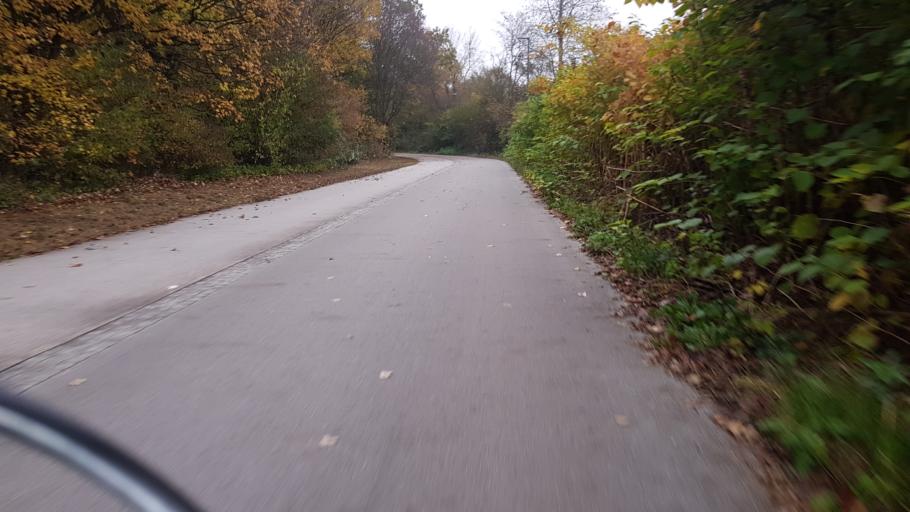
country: DE
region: Bavaria
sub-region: Upper Bavaria
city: Pasing
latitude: 48.1514
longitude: 11.4850
